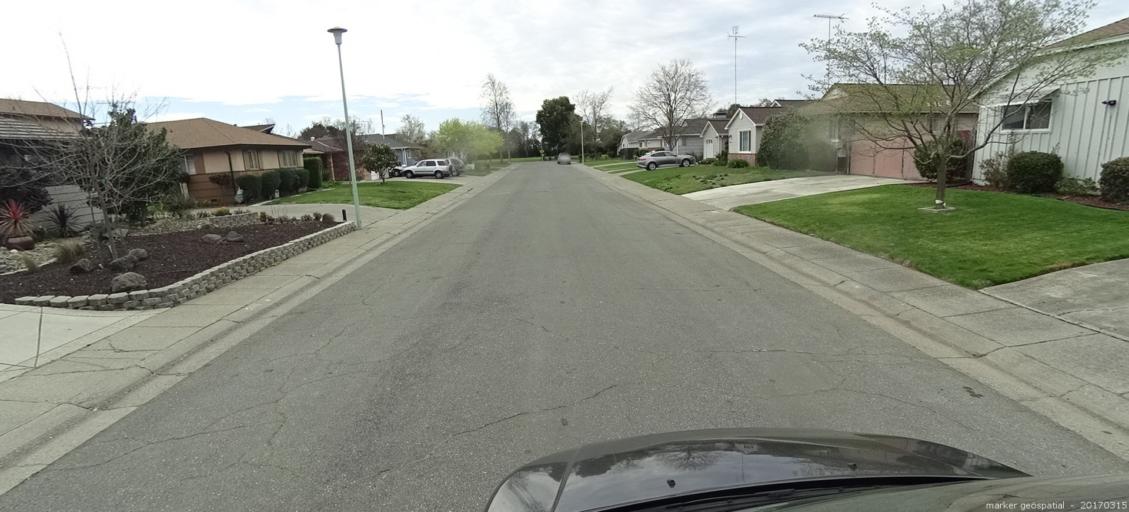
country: US
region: California
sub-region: Sacramento County
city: Parkway
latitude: 38.5233
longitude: -121.4885
